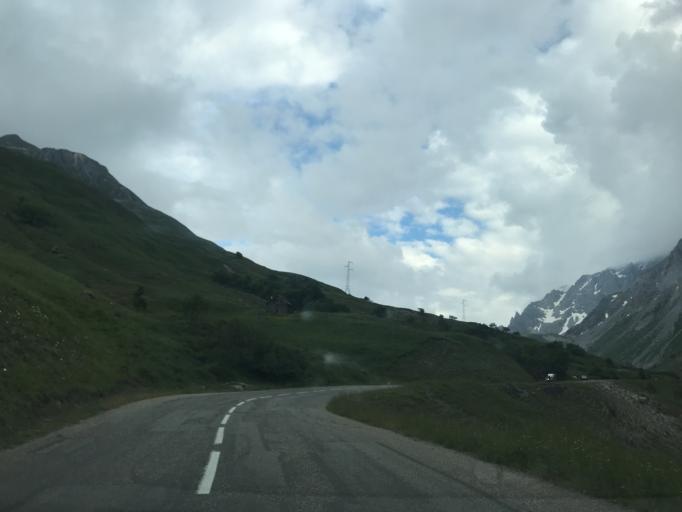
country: FR
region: Rhone-Alpes
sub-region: Departement de la Savoie
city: Valloire
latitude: 45.0991
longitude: 6.4291
